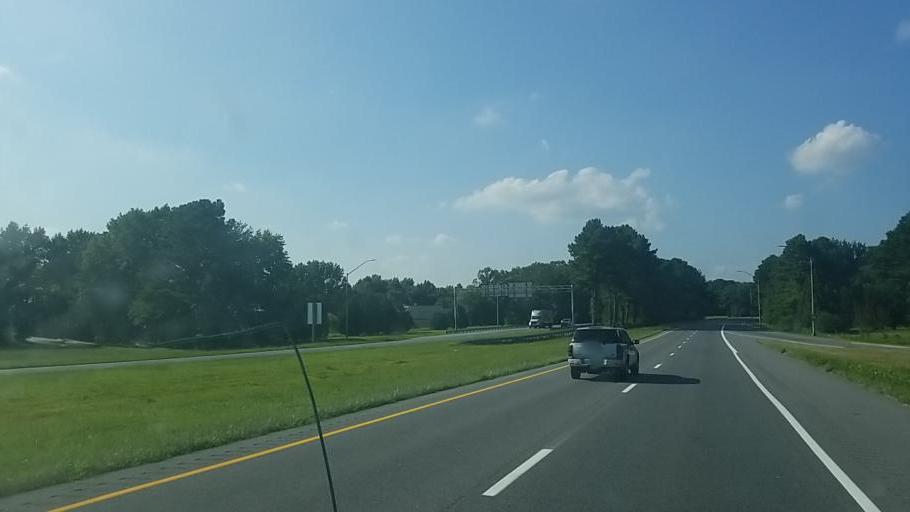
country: US
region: Maryland
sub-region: Worcester County
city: Berlin
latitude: 38.3452
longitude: -75.2141
